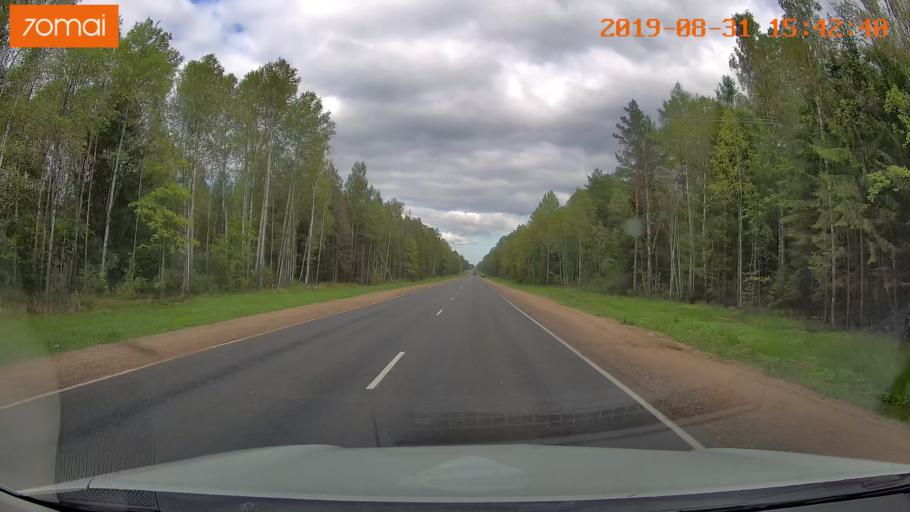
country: RU
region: Kaluga
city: Mosal'sk
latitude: 54.6478
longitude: 34.8918
